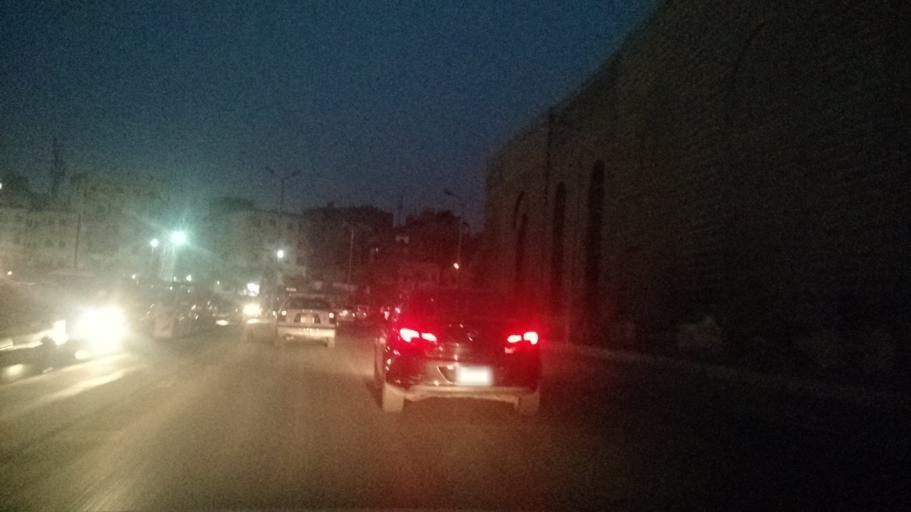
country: EG
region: Al Jizah
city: Al Jizah
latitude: 30.0209
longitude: 31.2384
